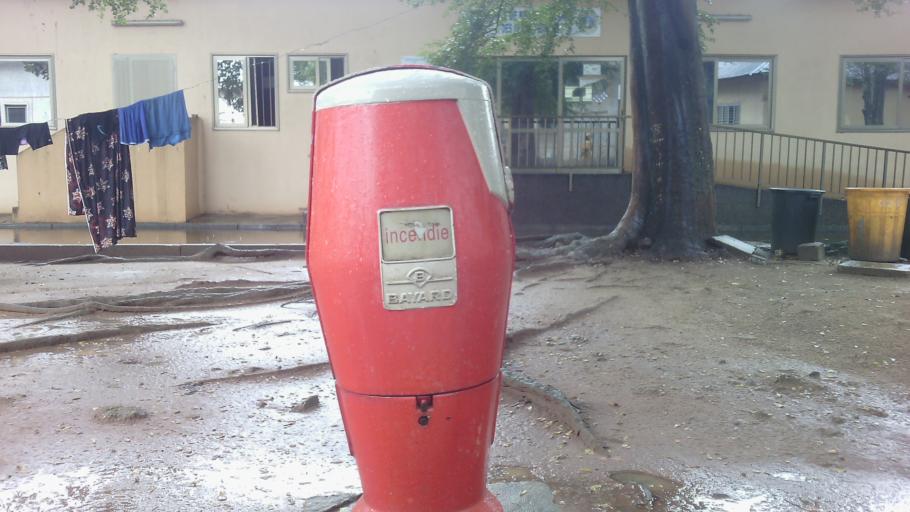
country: BJ
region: Queme
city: Porto-Novo
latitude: 6.4740
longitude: 2.6126
